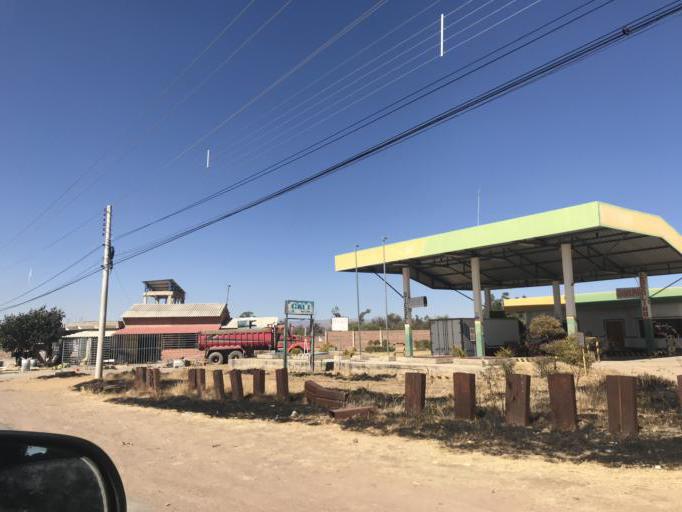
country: BO
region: Cochabamba
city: Tarata
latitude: -17.6113
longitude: -66.0168
